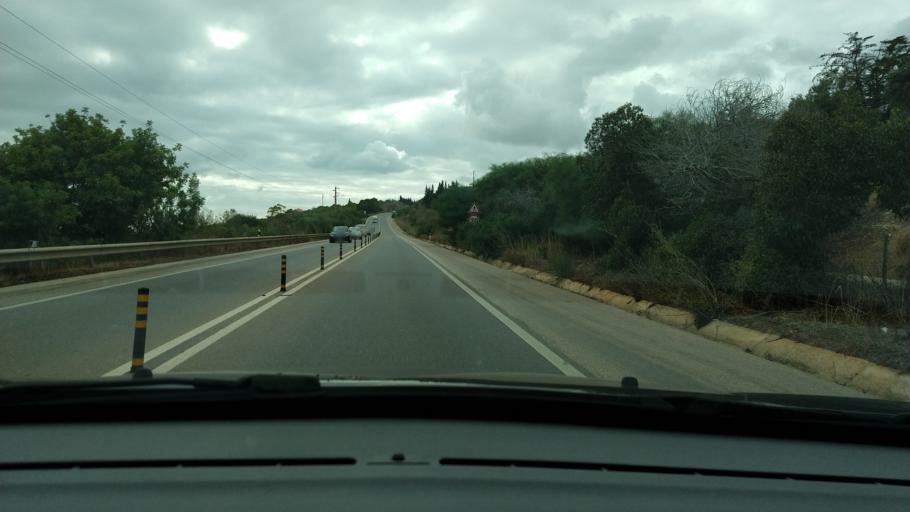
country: PT
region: Faro
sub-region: Lagos
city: Lagos
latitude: 37.1069
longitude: -8.7136
